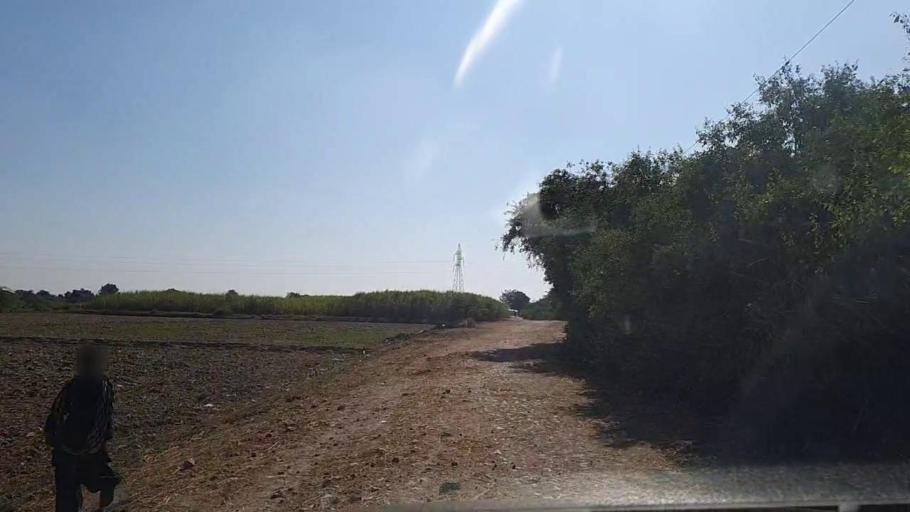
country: PK
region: Sindh
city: Mirpur Batoro
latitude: 24.6886
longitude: 68.1855
